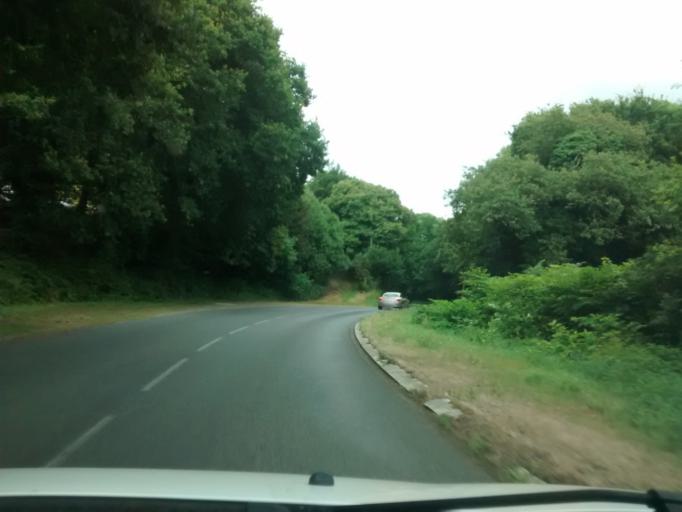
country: FR
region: Brittany
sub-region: Departement des Cotes-d'Armor
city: Trelevern
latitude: 48.7944
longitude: -3.3805
